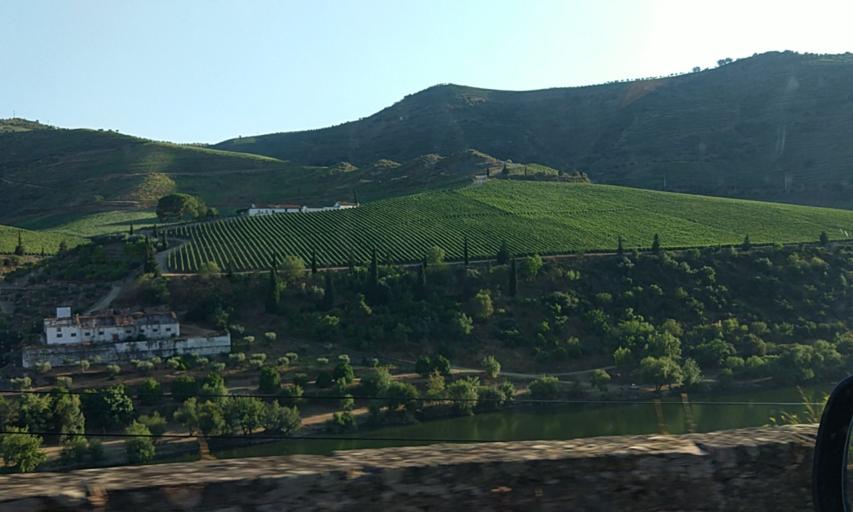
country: PT
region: Viseu
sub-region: Sao Joao da Pesqueira
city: Sao Joao da Pesqueira
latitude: 41.2119
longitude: -7.4239
